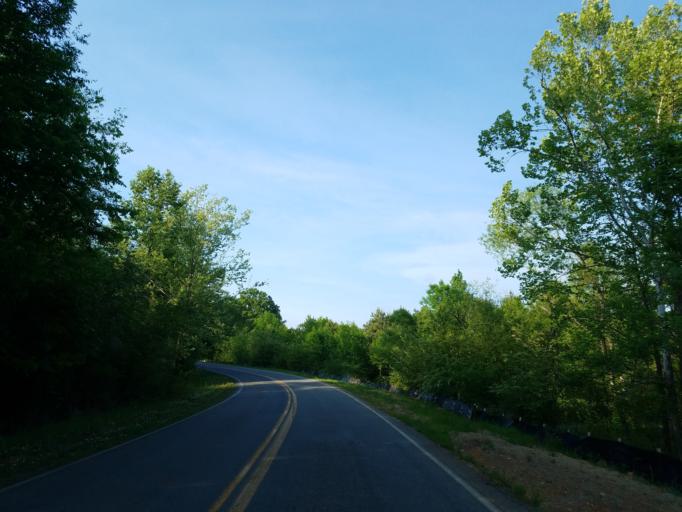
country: US
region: Georgia
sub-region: Floyd County
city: Shannon
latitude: 34.4751
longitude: -85.1377
